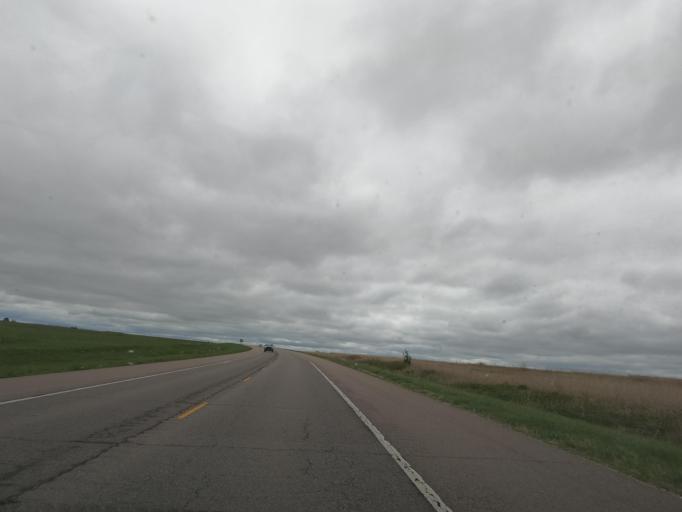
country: US
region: Kansas
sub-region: Greenwood County
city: Eureka
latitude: 37.6439
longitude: -96.4428
